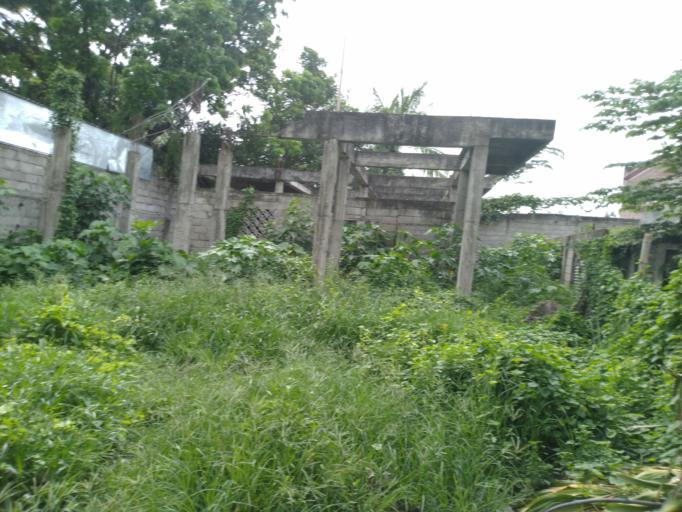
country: PH
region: Central Visayas
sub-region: Province of Negros Oriental
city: Dumaguete
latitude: 9.3052
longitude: 123.2983
